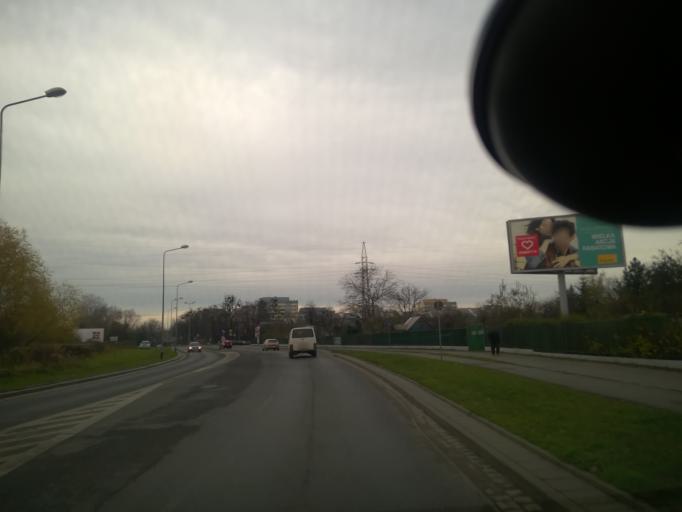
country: PL
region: Lower Silesian Voivodeship
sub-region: Powiat wroclawski
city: Wroclaw
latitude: 51.1178
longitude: 16.9839
